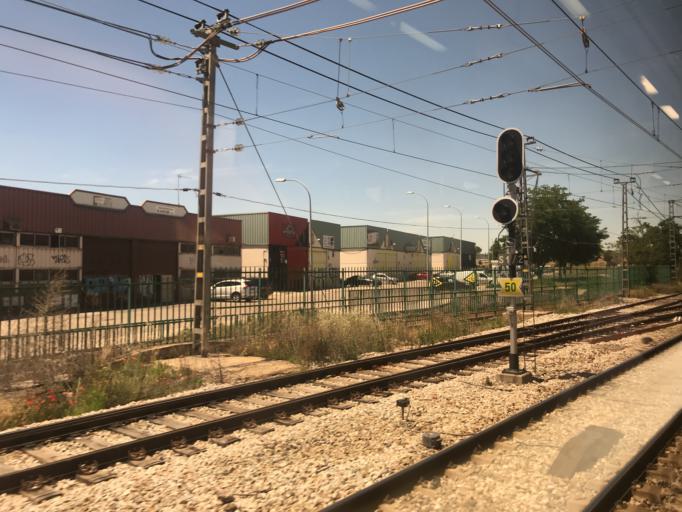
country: ES
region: Madrid
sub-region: Provincia de Madrid
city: Pinto
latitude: 40.2449
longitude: -3.7040
